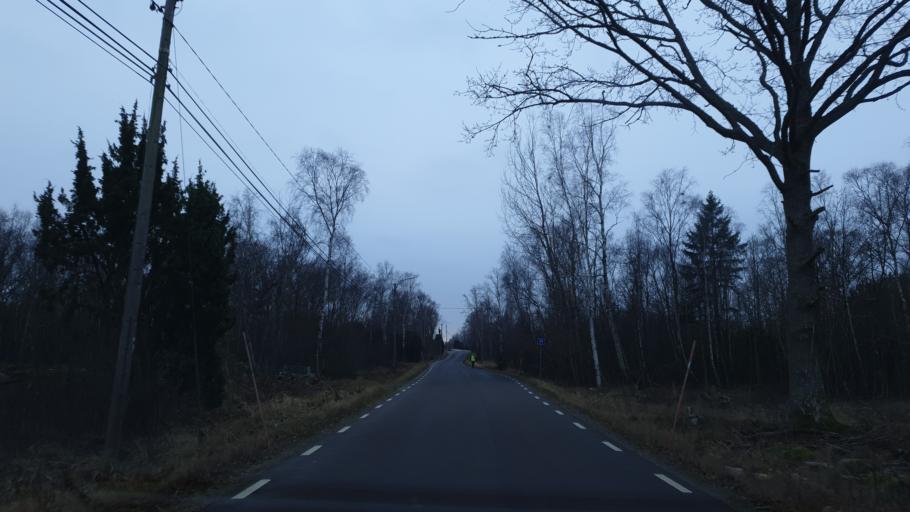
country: SE
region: Blekinge
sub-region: Karlskrona Kommun
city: Karlskrona
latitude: 56.1149
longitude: 15.6142
